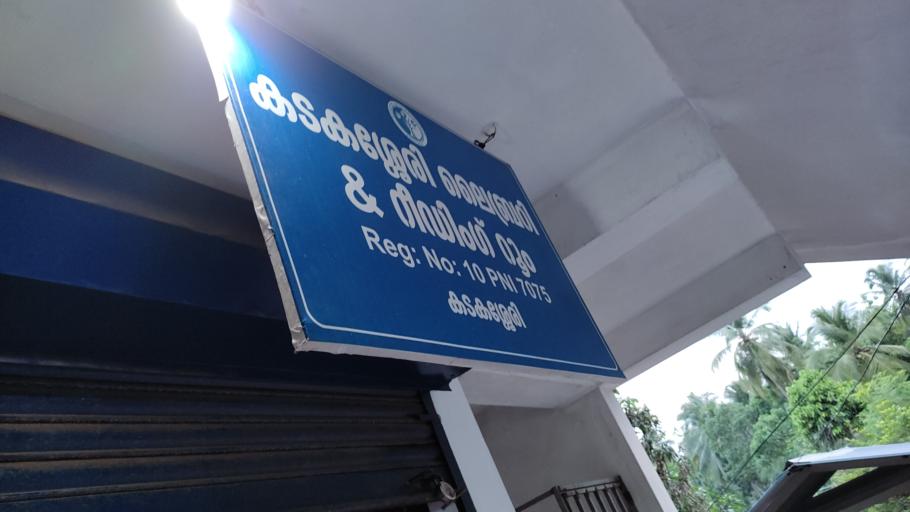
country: IN
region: Kerala
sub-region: Malappuram
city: Tirur
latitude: 10.8475
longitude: 75.9982
